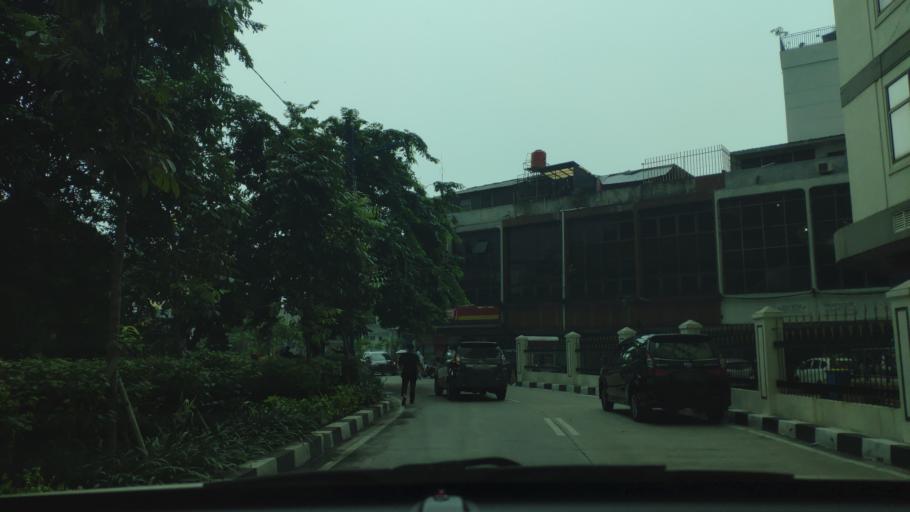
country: ID
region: Jakarta Raya
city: Jakarta
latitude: -6.1681
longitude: 106.8190
